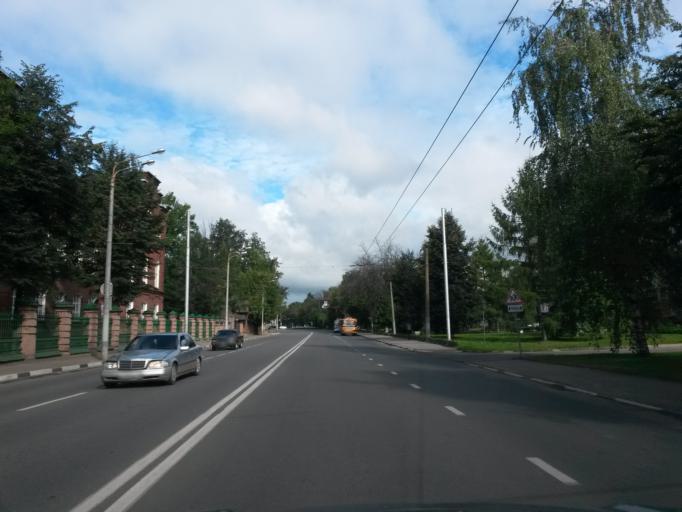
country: RU
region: Jaroslavl
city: Yaroslavl
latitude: 57.6377
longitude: 39.8786
